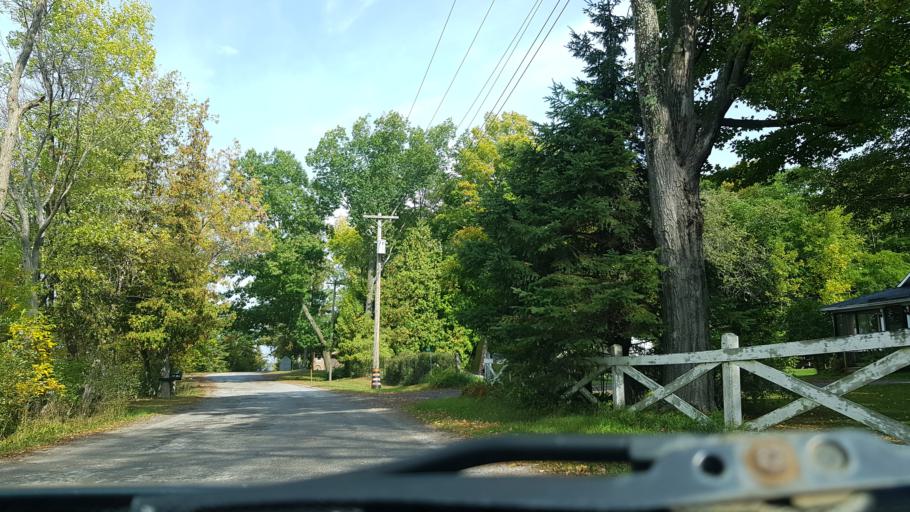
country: CA
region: Ontario
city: Orillia
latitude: 44.6512
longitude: -79.1032
